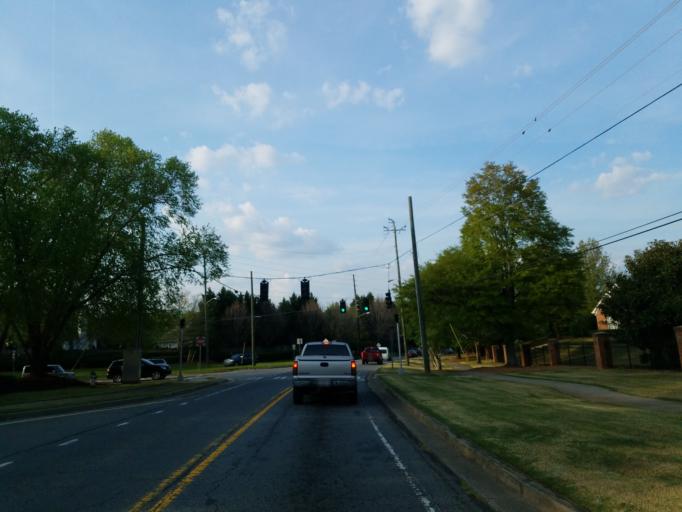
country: US
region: Georgia
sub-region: Fulton County
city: Roswell
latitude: 34.0757
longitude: -84.3609
